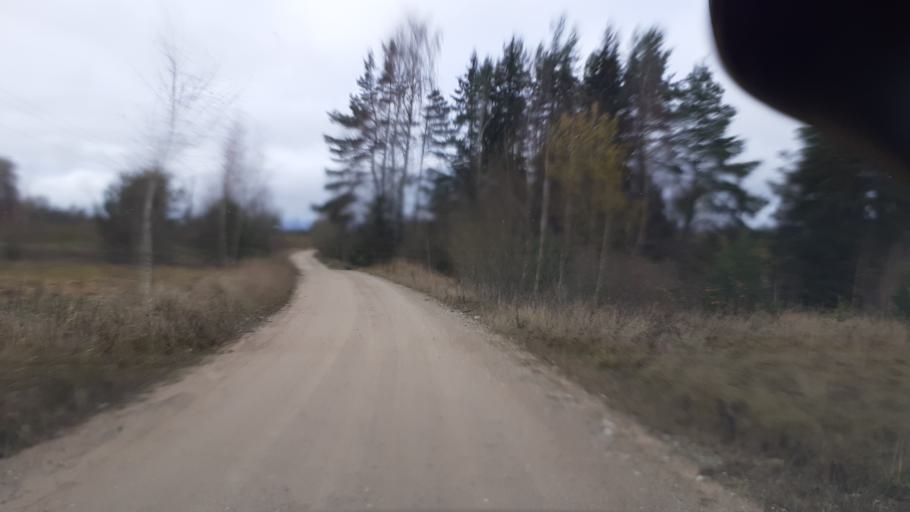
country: LV
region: Kuldigas Rajons
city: Kuldiga
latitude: 57.0395
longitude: 21.8794
